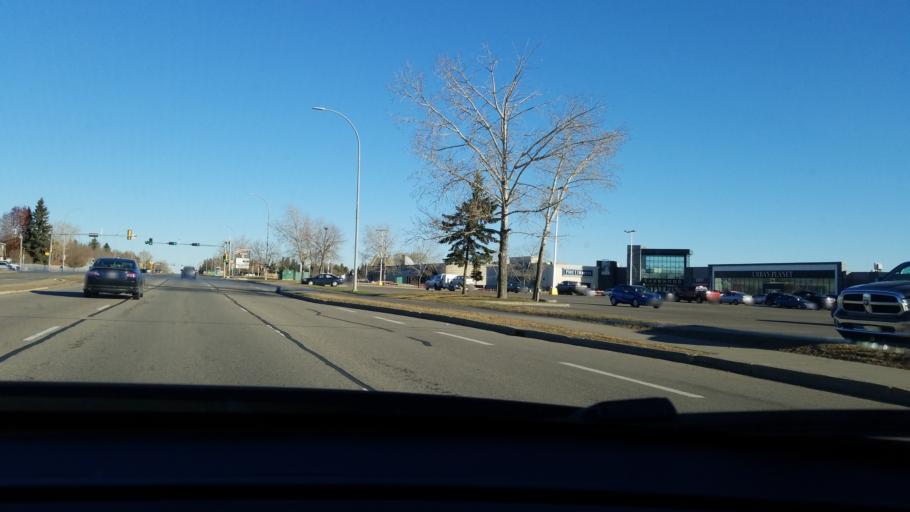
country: CA
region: Alberta
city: Sherwood Park
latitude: 53.5291
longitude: -113.2955
